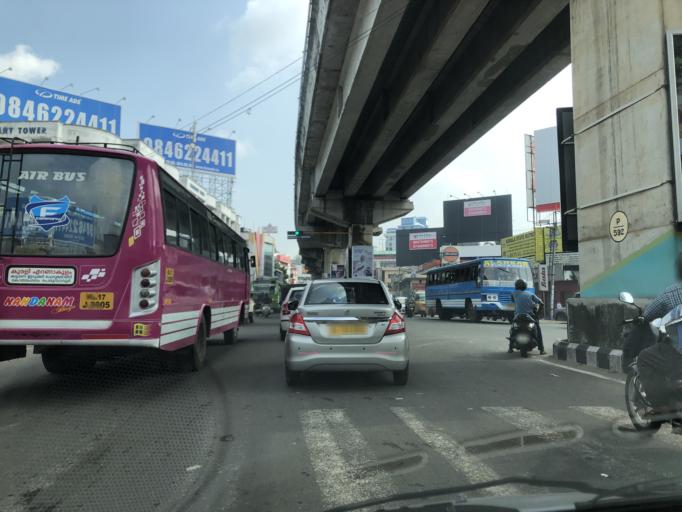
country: IN
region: Kerala
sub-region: Ernakulam
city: Cochin
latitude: 9.9949
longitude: 76.2919
